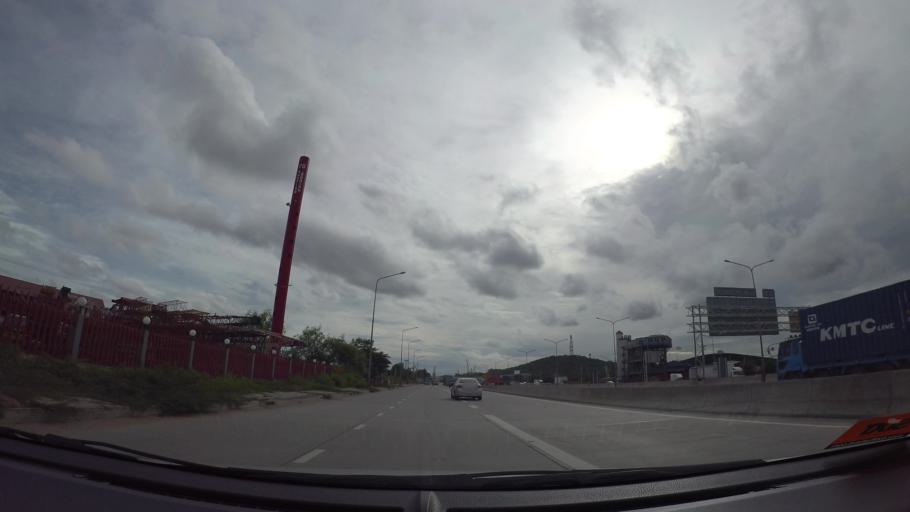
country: TH
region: Chon Buri
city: Ban Talat Bueng
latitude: 13.1138
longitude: 100.9661
